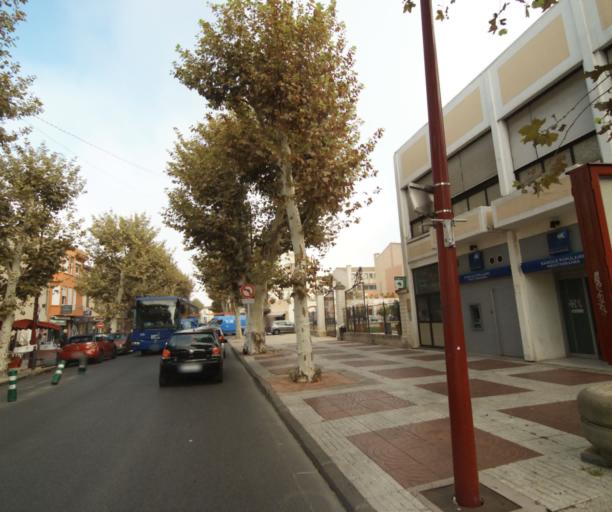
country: FR
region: Provence-Alpes-Cote d'Azur
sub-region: Departement des Bouches-du-Rhone
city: Marignane
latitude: 43.4161
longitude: 5.2165
